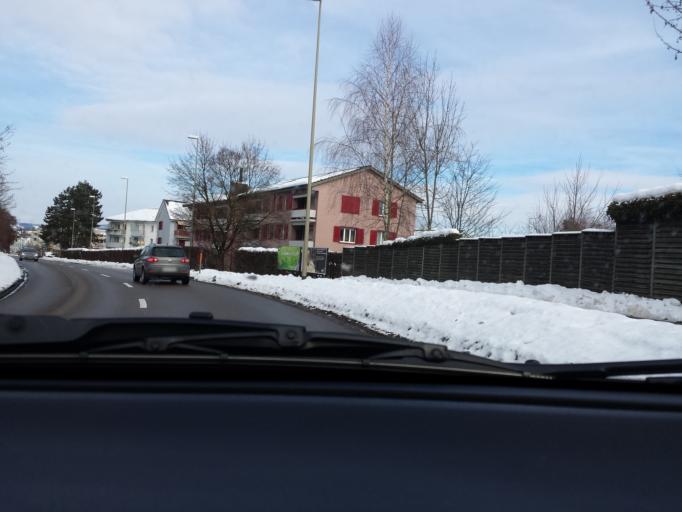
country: CH
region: Zurich
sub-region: Bezirk Hinwil
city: Wetzikon / Unter-Wetzikon
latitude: 47.3119
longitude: 8.7936
